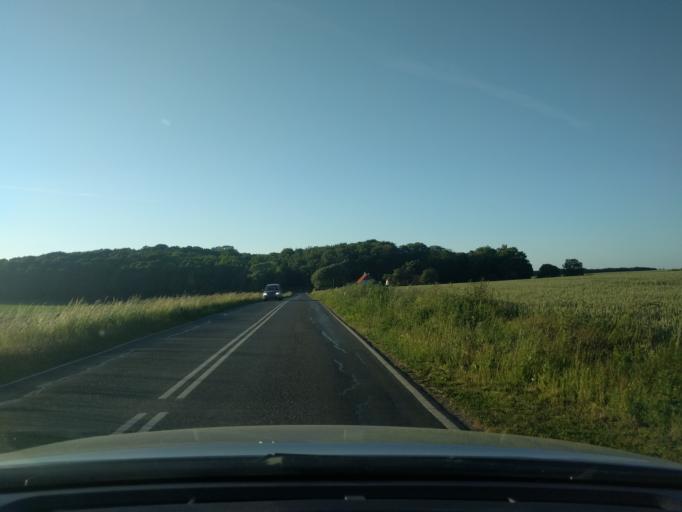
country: DK
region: South Denmark
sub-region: Kerteminde Kommune
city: Kerteminde
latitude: 55.5268
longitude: 10.6528
